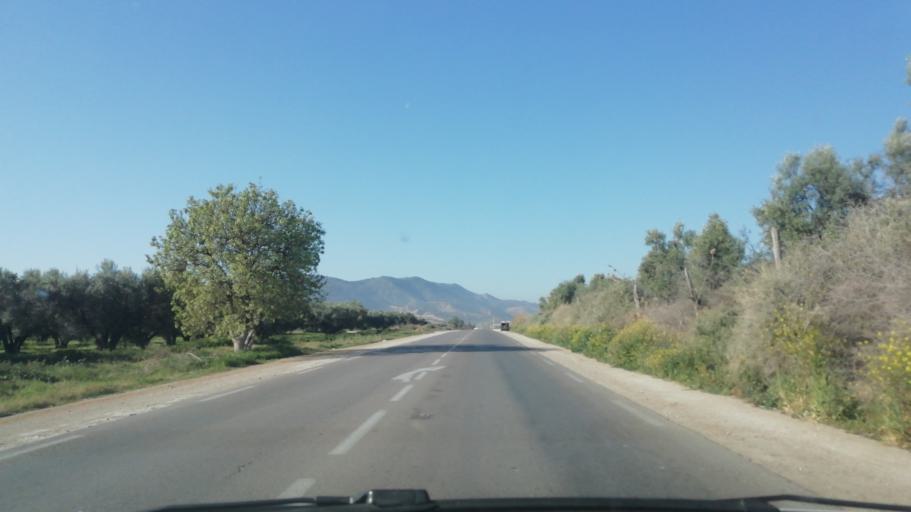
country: DZ
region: Mascara
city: Sig
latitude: 35.5403
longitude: -0.1314
